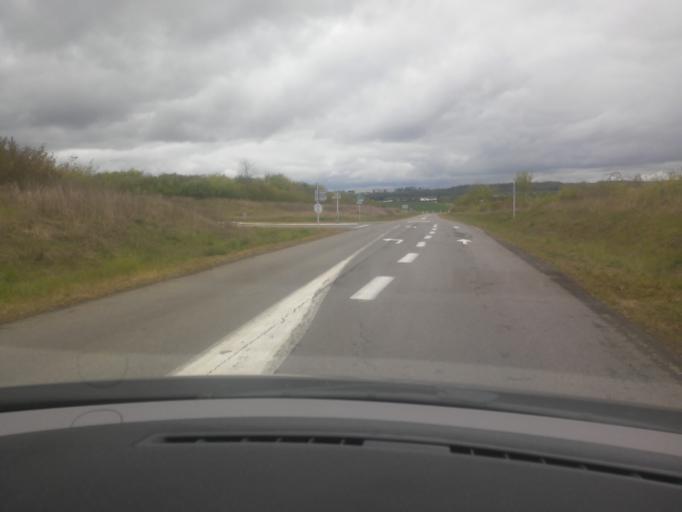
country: FR
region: Lorraine
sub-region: Departement de la Moselle
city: Mecleuves
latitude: 49.0503
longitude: 6.2569
